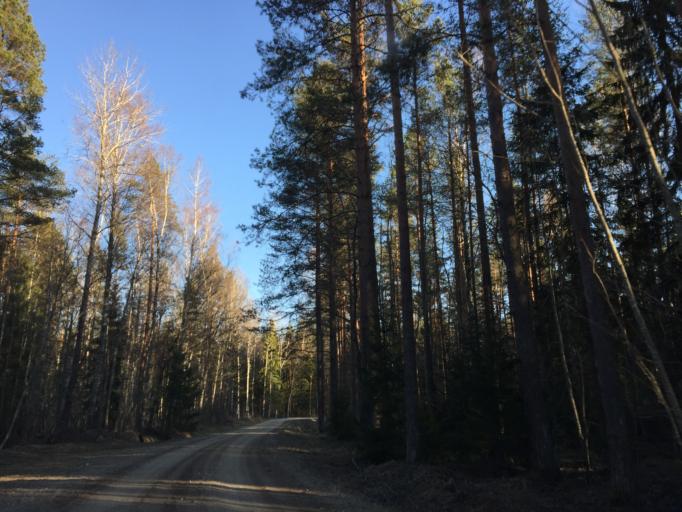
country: EE
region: Ida-Virumaa
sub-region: Sillamaee linn
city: Sillamae
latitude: 59.1461
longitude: 27.8083
